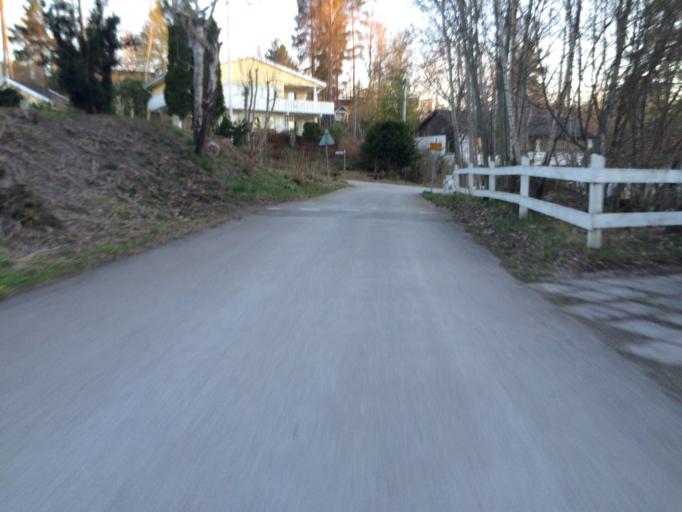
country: SE
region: Soedermanland
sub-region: Eskilstuna Kommun
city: Kvicksund
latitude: 59.4509
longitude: 16.3369
